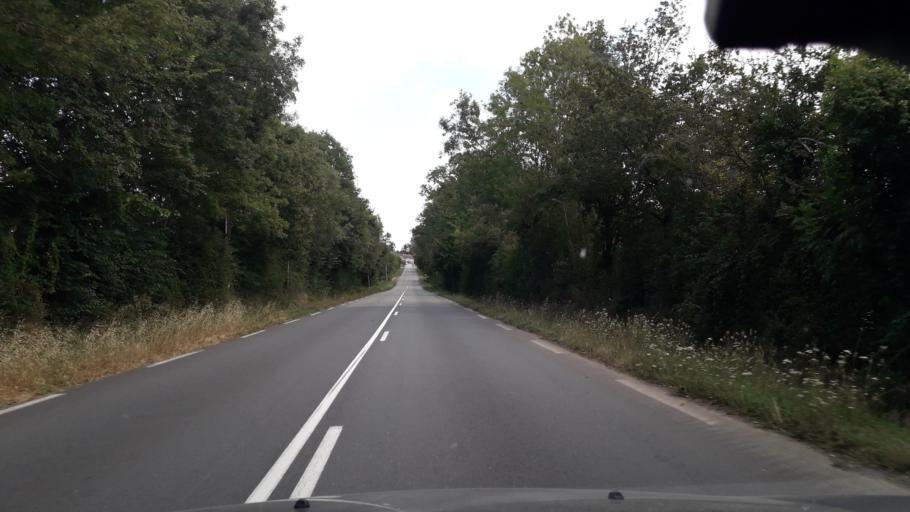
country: FR
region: Limousin
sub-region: Departement de la Haute-Vienne
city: Bussiere-Poitevine
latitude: 46.1070
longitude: 0.8988
